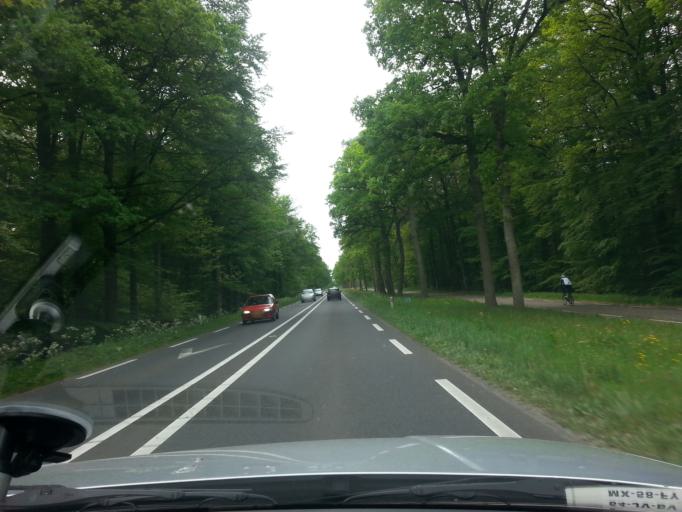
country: NL
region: Overijssel
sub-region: Gemeente Oldenzaal
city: Oldenzaal
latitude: 52.3352
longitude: 6.9565
